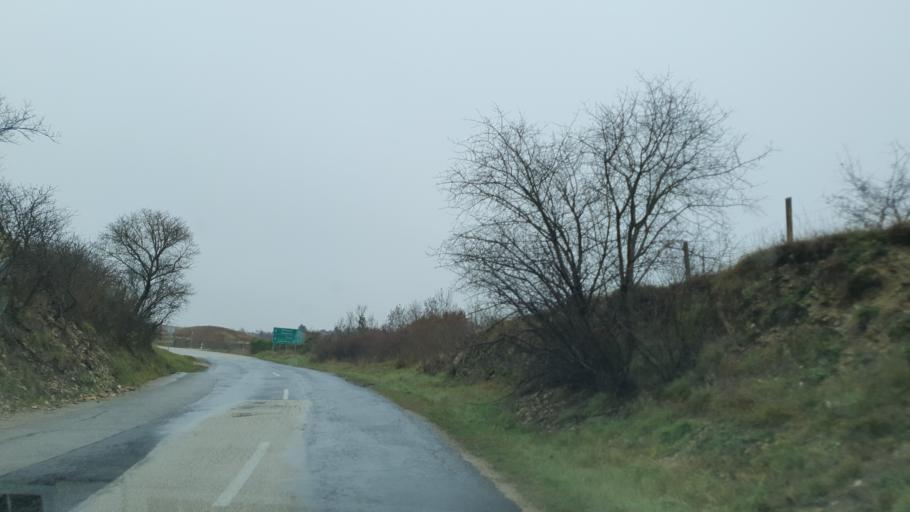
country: HU
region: Veszprem
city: Hajmasker
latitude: 47.1388
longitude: 18.0219
